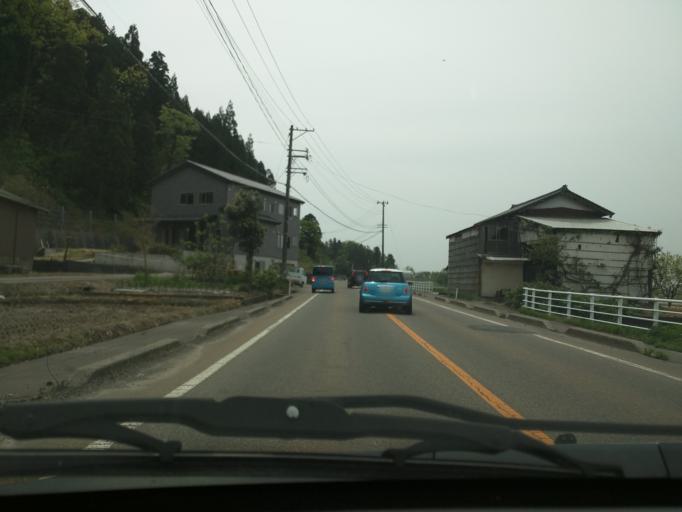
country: JP
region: Niigata
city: Mitsuke
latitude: 37.5635
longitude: 138.9346
